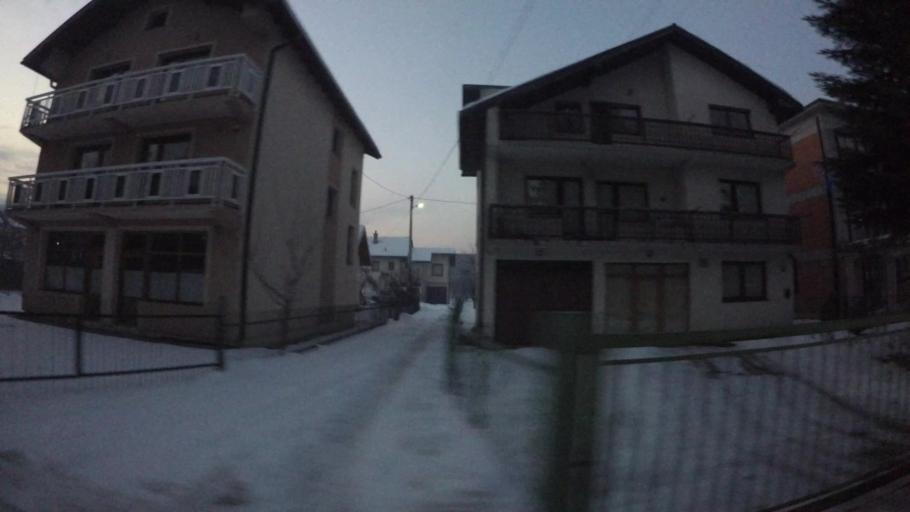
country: BA
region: Federation of Bosnia and Herzegovina
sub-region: Kanton Sarajevo
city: Sarajevo
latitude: 43.8345
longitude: 18.3213
